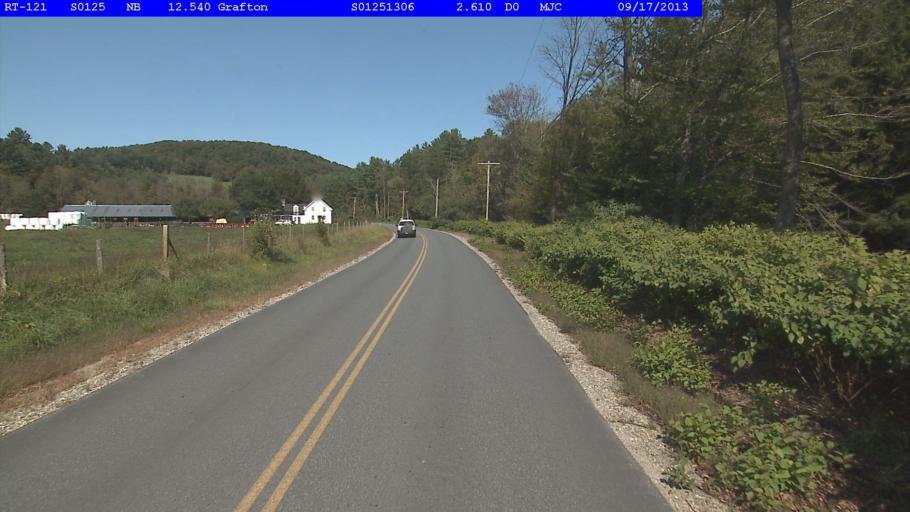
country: US
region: Vermont
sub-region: Windsor County
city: Chester
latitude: 43.1758
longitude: -72.5819
